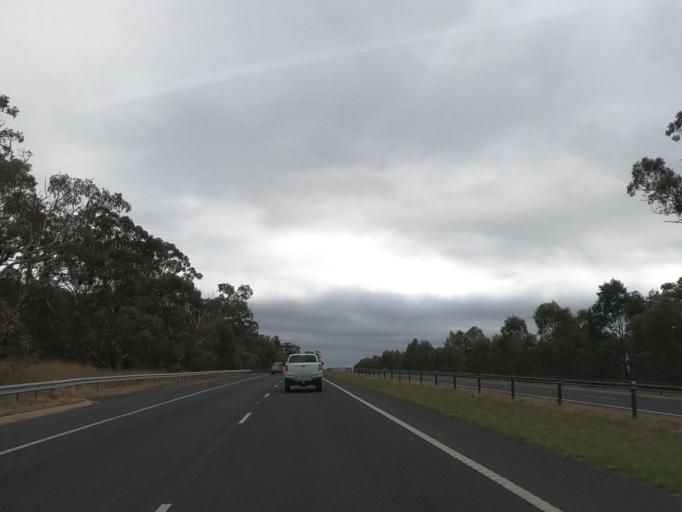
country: AU
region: Victoria
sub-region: Mount Alexander
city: Castlemaine
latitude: -37.0320
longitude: 144.2752
